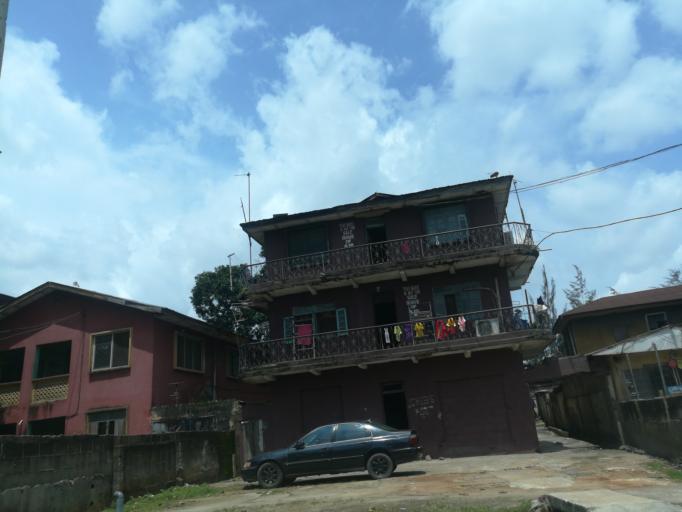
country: NG
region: Lagos
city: Somolu
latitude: 6.5394
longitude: 3.3634
